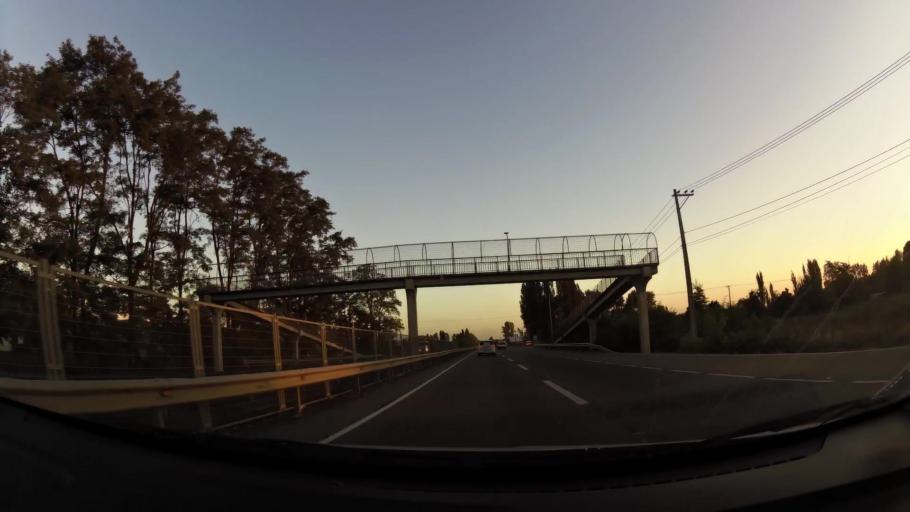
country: CL
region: Maule
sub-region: Provincia de Linares
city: San Javier
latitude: -35.7192
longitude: -71.6803
